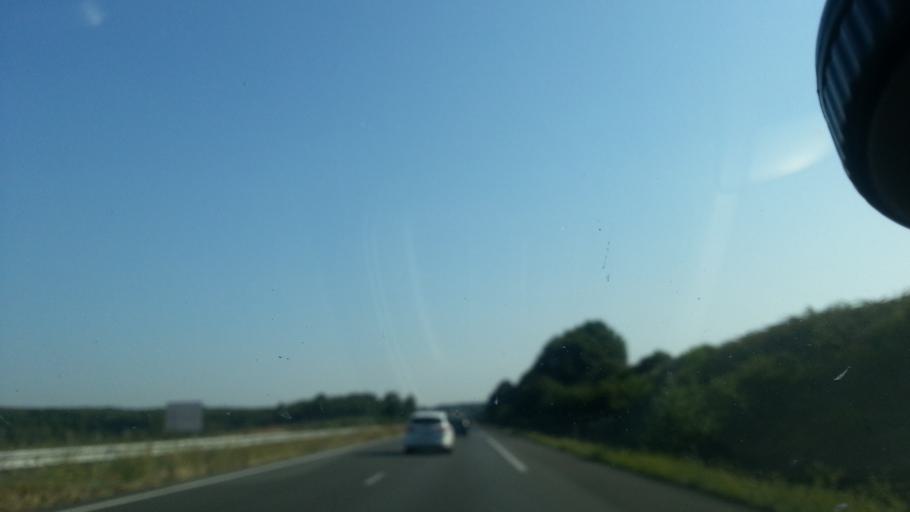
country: FR
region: Poitou-Charentes
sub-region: Departement de la Vienne
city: Antran
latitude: 46.9172
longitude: 0.5310
